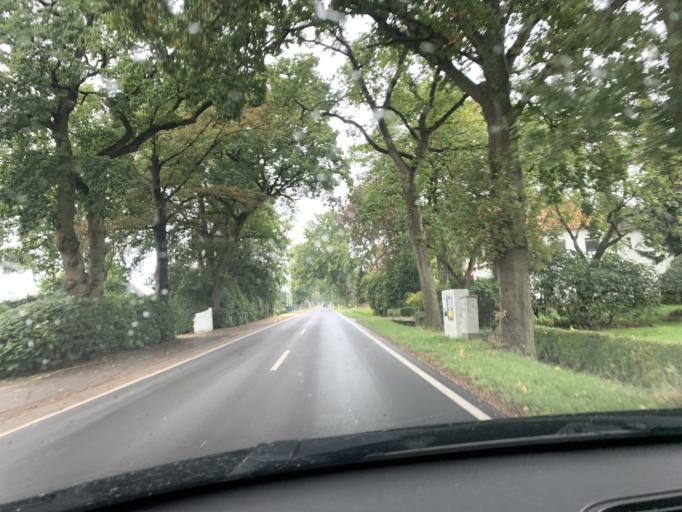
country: DE
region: Lower Saxony
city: Bad Zwischenahn
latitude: 53.1586
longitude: 8.0847
